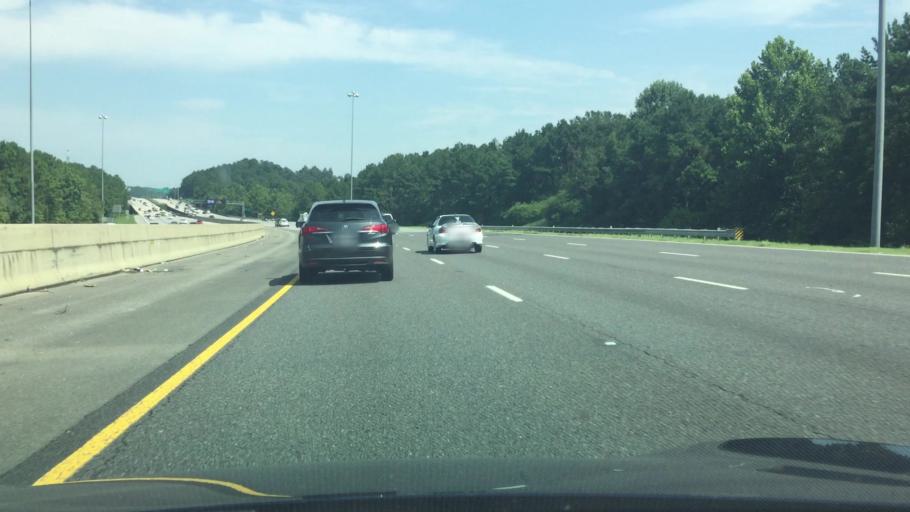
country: US
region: Alabama
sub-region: Shelby County
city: Indian Springs Village
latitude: 33.3658
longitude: -86.7763
